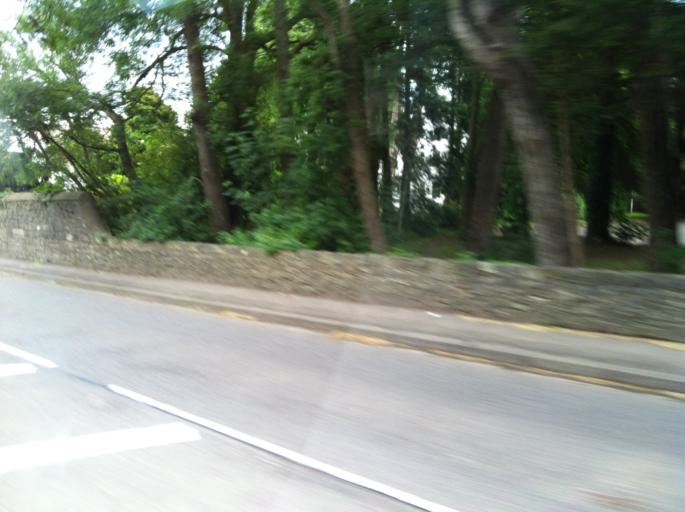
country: GB
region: Wales
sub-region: Bridgend county borough
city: Bridgend
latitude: 51.4916
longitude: -3.5784
